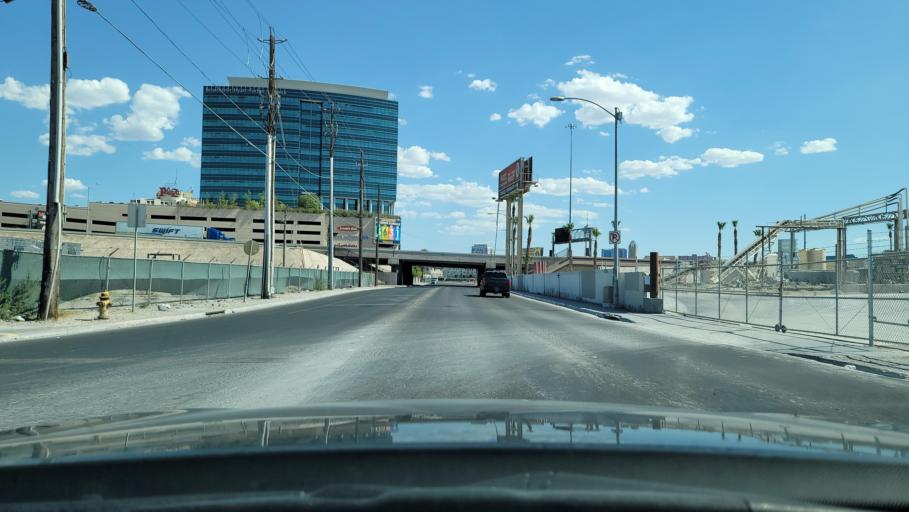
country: US
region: Nevada
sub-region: Clark County
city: Las Vegas
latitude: 36.1764
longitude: -115.1493
